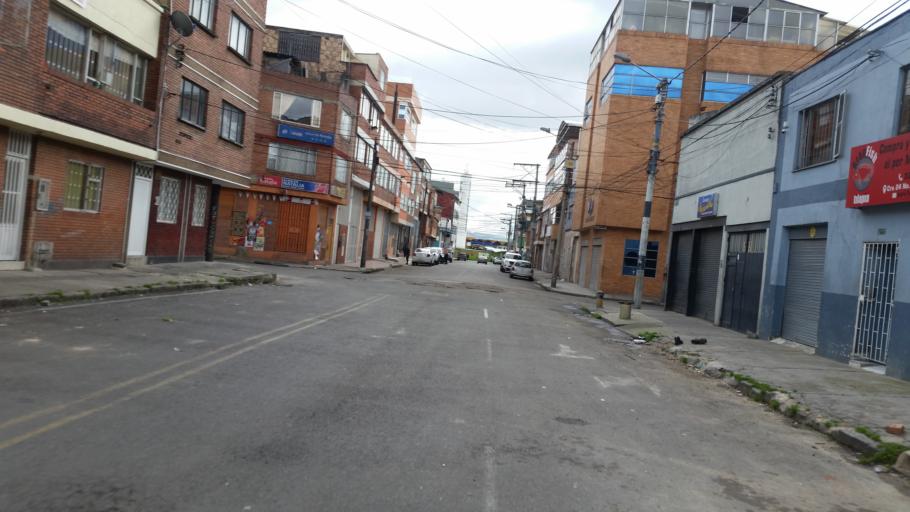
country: CO
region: Bogota D.C.
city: Bogota
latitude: 4.6179
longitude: -74.0815
